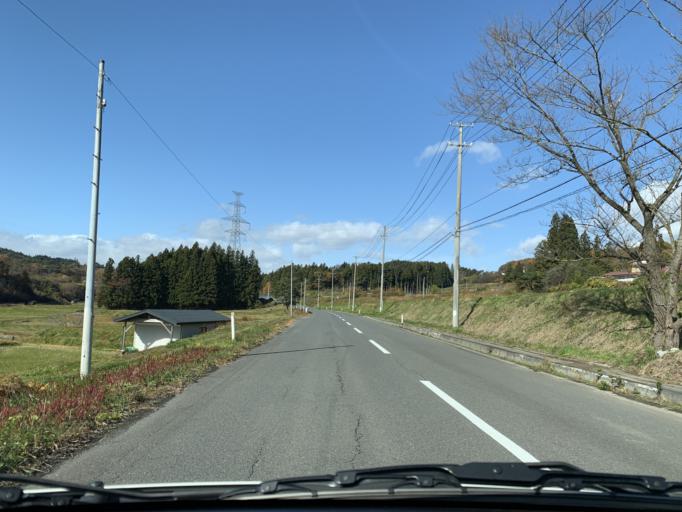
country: JP
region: Iwate
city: Ichinoseki
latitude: 39.0243
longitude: 141.1113
